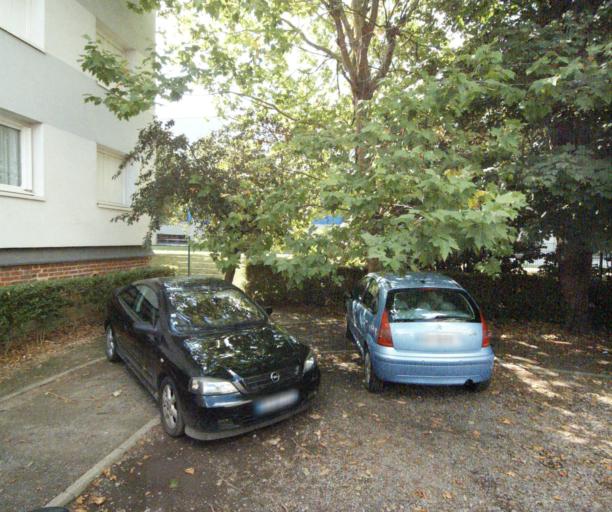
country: FR
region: Nord-Pas-de-Calais
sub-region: Departement du Nord
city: Mons-en-Baroeul
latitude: 50.6241
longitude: 3.1181
